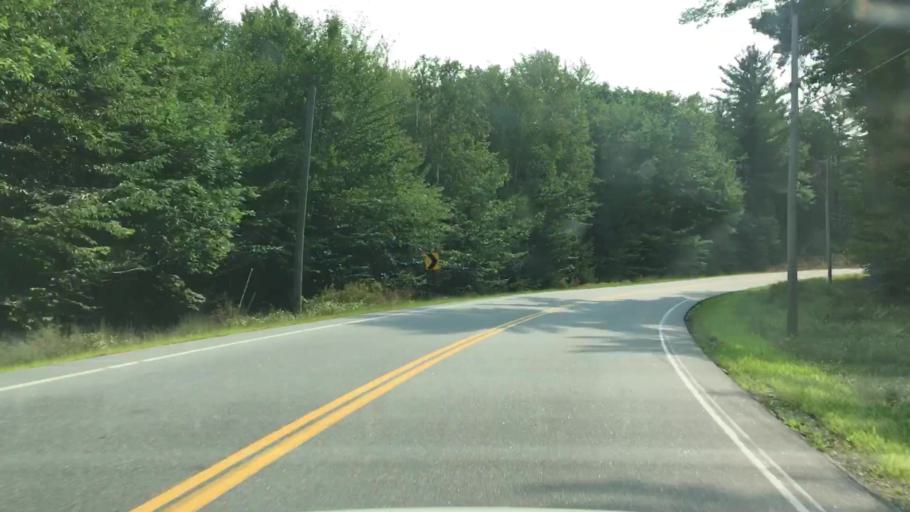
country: US
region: Maine
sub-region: Oxford County
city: Buckfield
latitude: 44.2770
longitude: -70.3816
